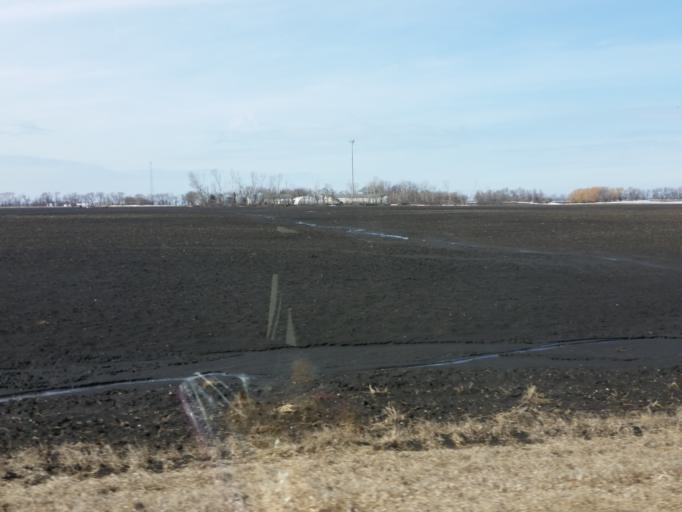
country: US
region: North Dakota
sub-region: Walsh County
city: Grafton
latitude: 48.2994
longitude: -97.2110
